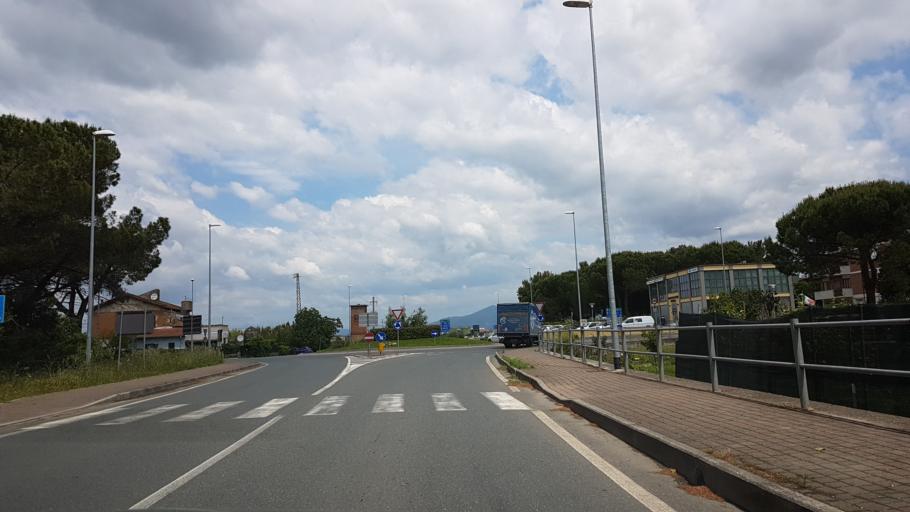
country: IT
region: Tuscany
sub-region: Provincia di Livorno
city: Collesalvetti
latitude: 43.5879
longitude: 10.4709
